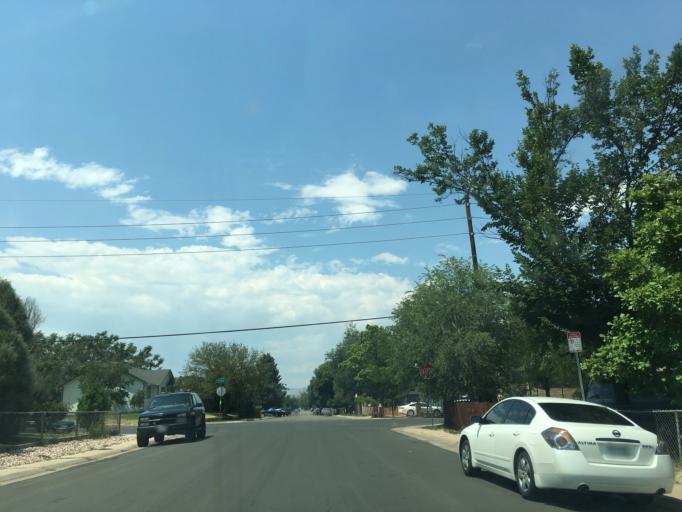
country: US
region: Colorado
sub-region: Jefferson County
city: Lakewood
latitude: 39.7032
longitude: -105.0294
